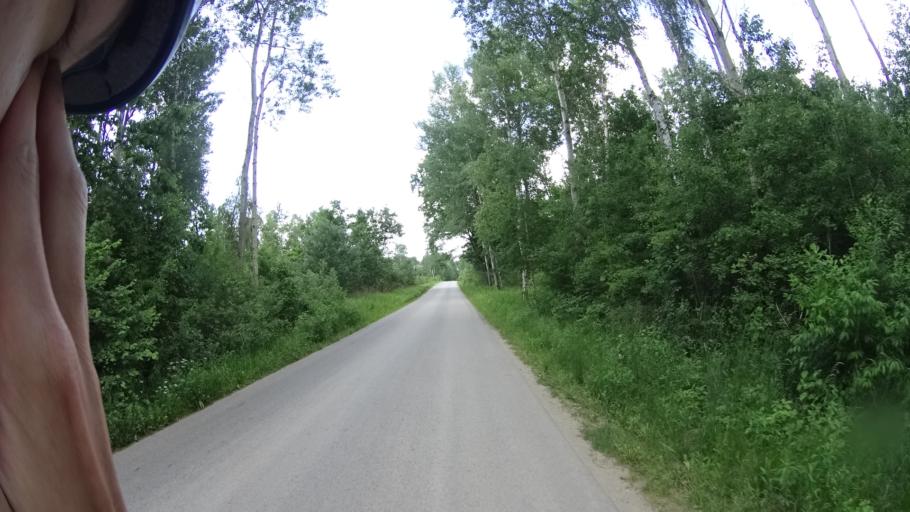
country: PL
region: Masovian Voivodeship
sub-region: Powiat pruszkowski
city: Nadarzyn
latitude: 52.0693
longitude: 20.8194
